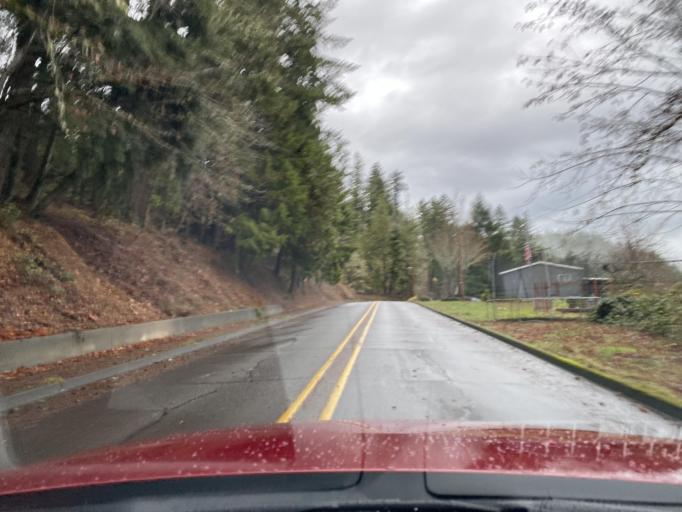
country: US
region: Oregon
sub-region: Lane County
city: Oakridge
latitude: 43.7513
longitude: -122.4874
